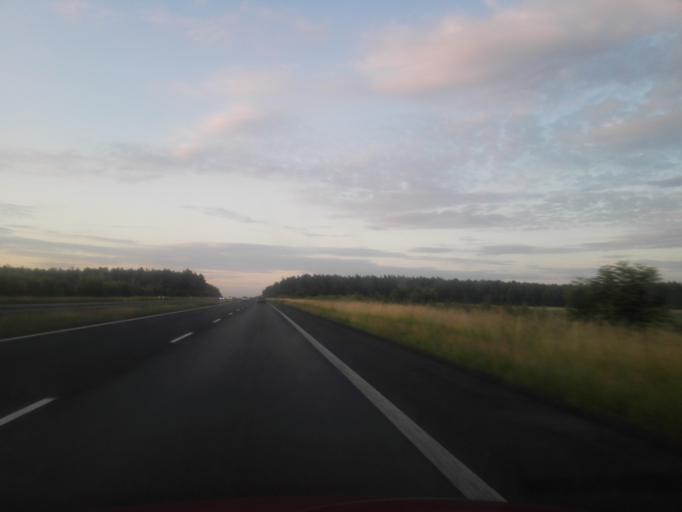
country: PL
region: Silesian Voivodeship
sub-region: Powiat czestochowski
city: Borowno
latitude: 50.9774
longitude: 19.2739
